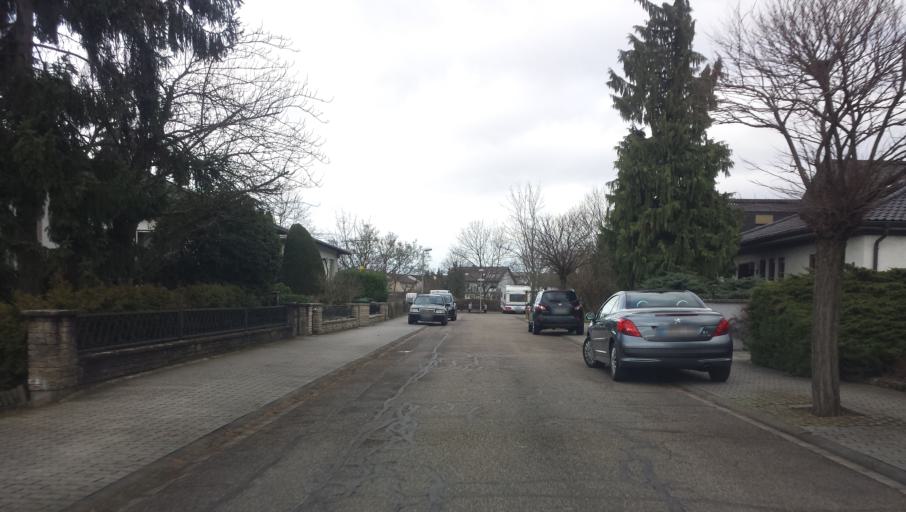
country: DE
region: Baden-Wuerttemberg
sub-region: Karlsruhe Region
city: Ketsch
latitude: 49.3755
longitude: 8.5415
